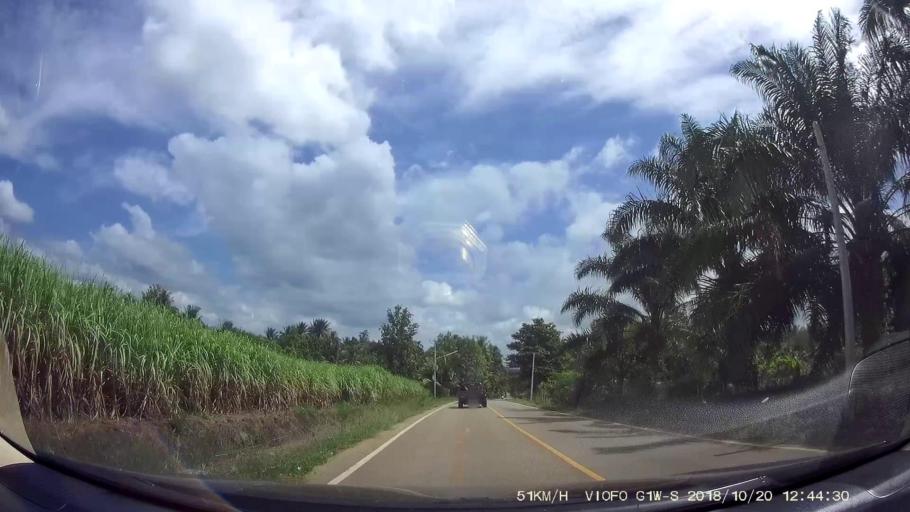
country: TH
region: Chaiyaphum
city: Khon San
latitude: 16.5387
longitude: 101.8694
